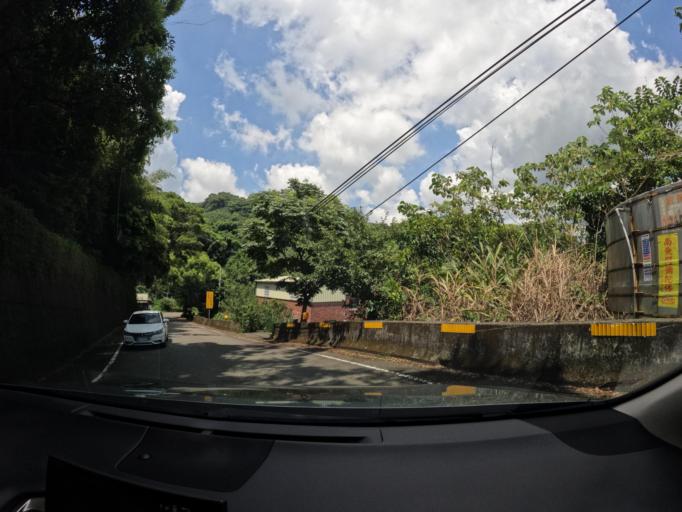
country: TW
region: Taiwan
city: Fengyuan
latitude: 24.3820
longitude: 120.8290
